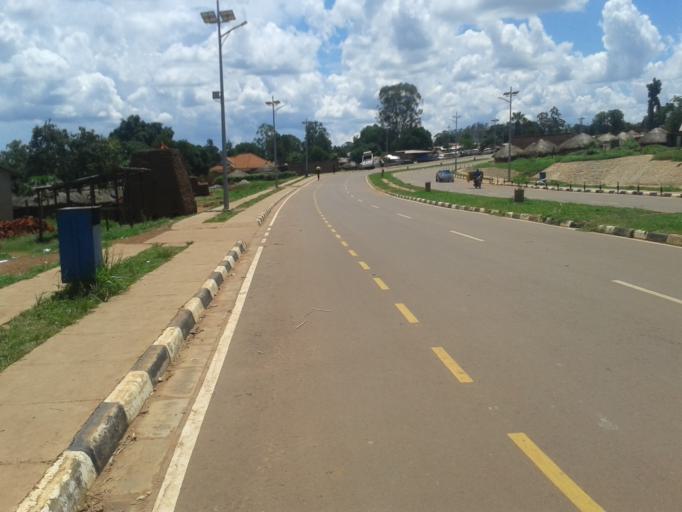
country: UG
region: Northern Region
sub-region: Gulu District
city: Gulu
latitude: 2.7637
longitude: 32.2943
